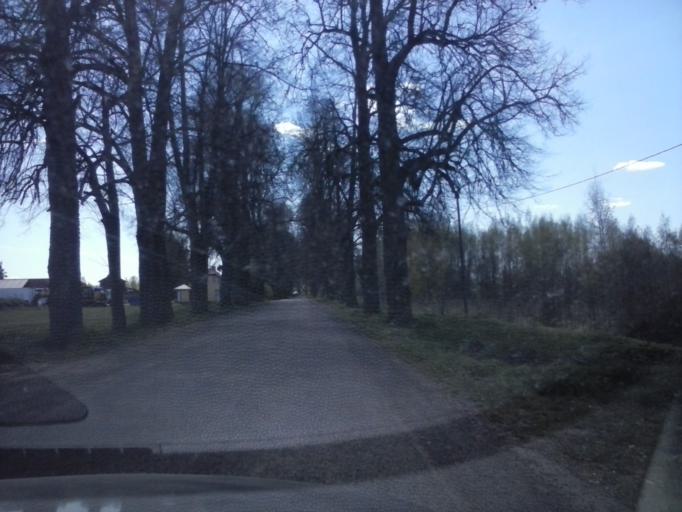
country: EE
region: Valgamaa
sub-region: Torva linn
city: Torva
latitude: 58.2310
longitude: 25.8905
